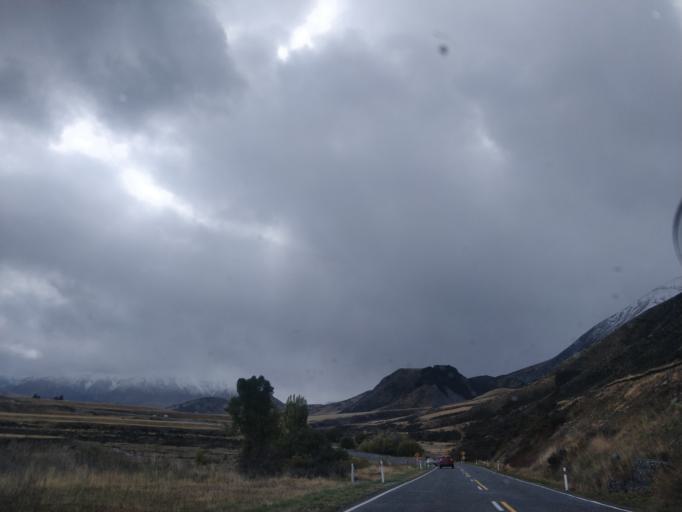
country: NZ
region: Canterbury
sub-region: Ashburton District
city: Methven
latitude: -43.2472
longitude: 171.7227
